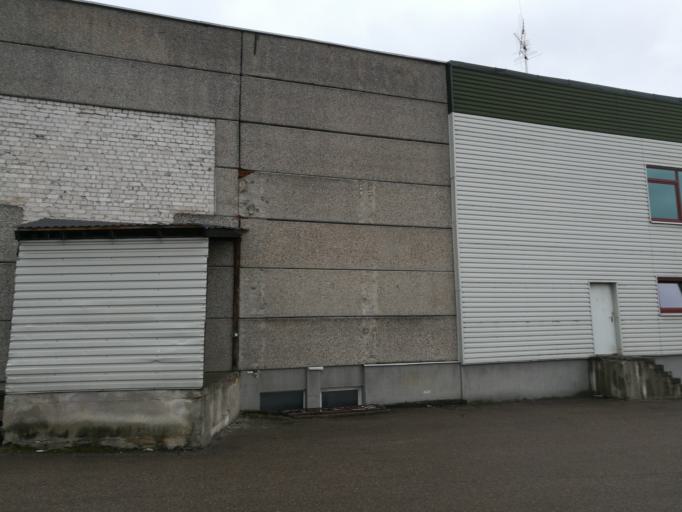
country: LT
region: Vilnius County
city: Vilkpede
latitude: 54.6596
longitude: 25.2287
